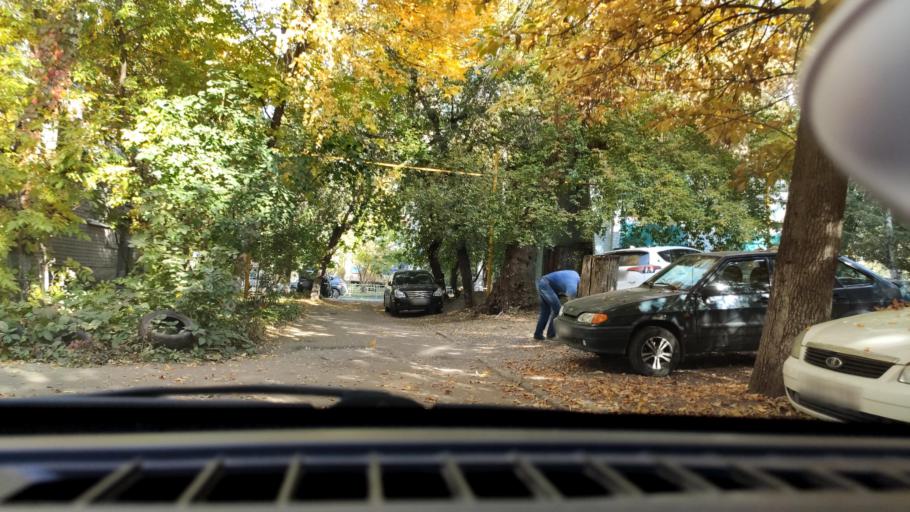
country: RU
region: Samara
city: Samara
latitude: 53.2136
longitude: 50.1623
